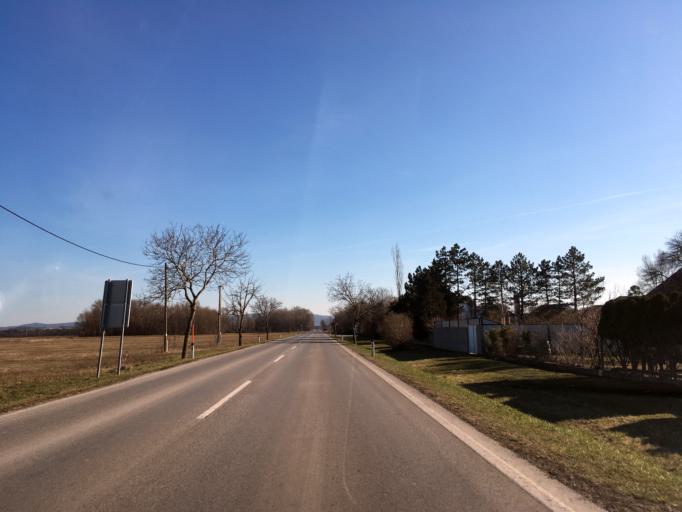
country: AT
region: Lower Austria
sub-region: Politischer Bezirk Baden
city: Ebreichsdorf
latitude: 47.9450
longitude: 16.4111
